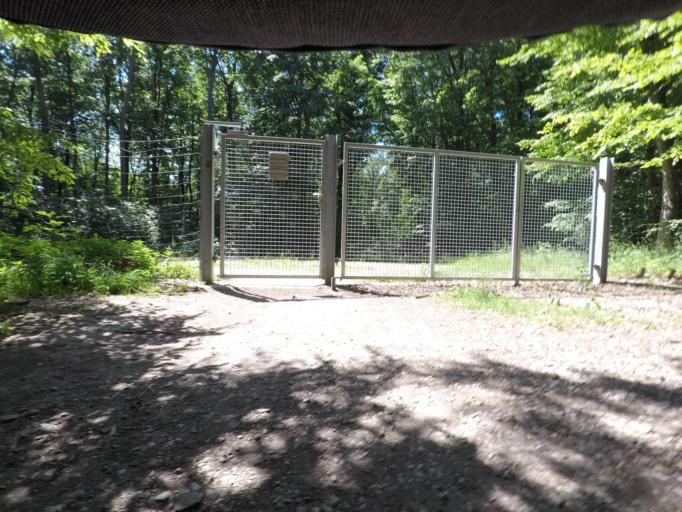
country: AT
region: Lower Austria
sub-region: Politischer Bezirk Modling
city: Perchtoldsdorf
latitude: 48.1779
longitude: 16.2462
